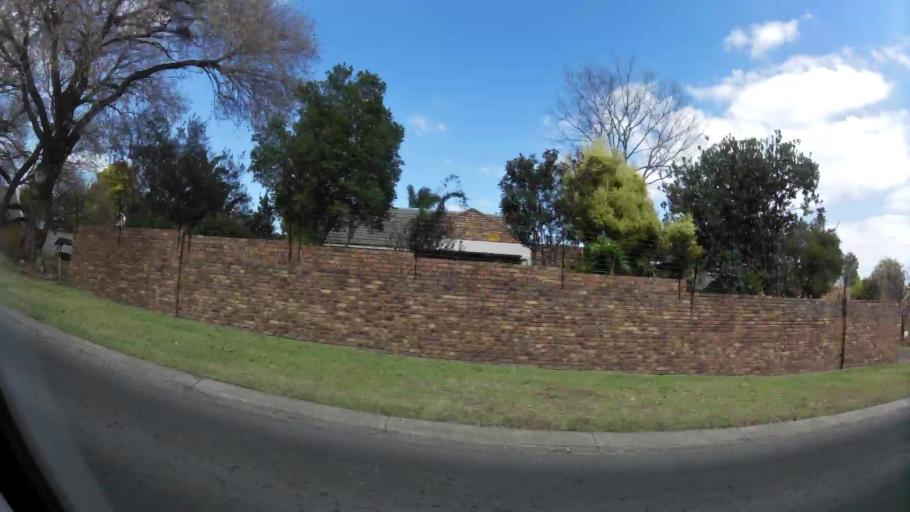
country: ZA
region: Gauteng
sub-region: City of Johannesburg Metropolitan Municipality
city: Midrand
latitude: -26.0307
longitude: 28.0776
